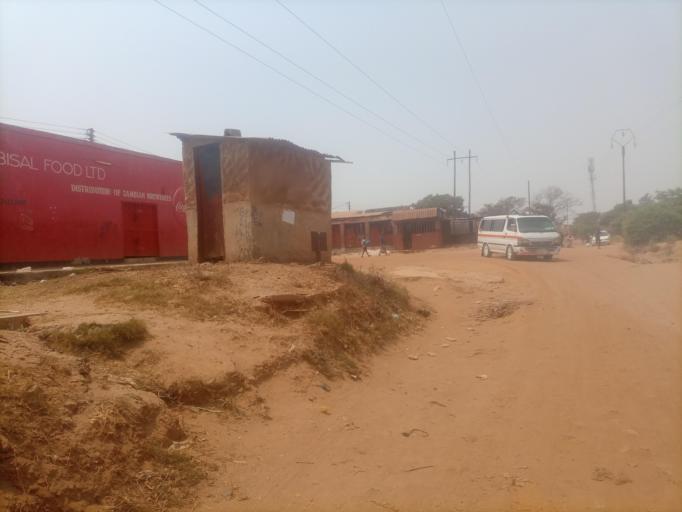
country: ZM
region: Lusaka
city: Lusaka
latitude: -15.3972
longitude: 28.3684
